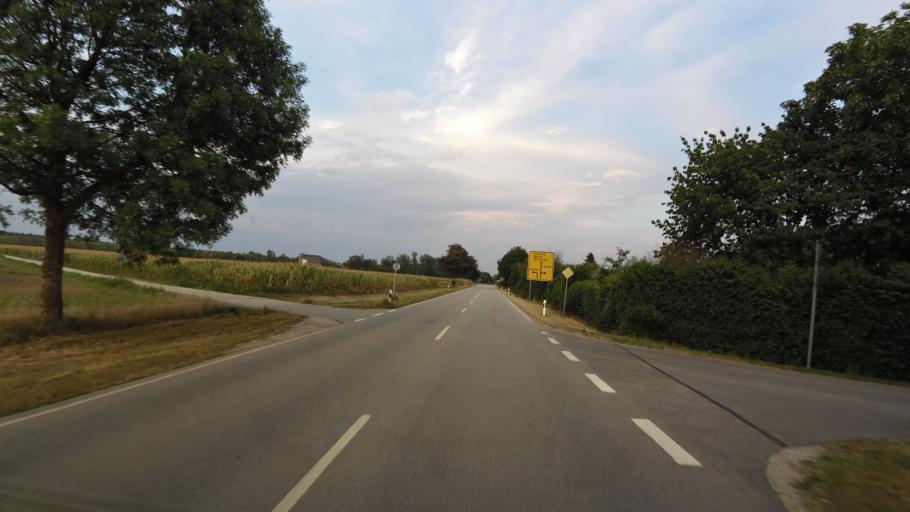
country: DE
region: Bavaria
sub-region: Lower Bavaria
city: Kirchham
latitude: 48.3508
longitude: 13.2673
